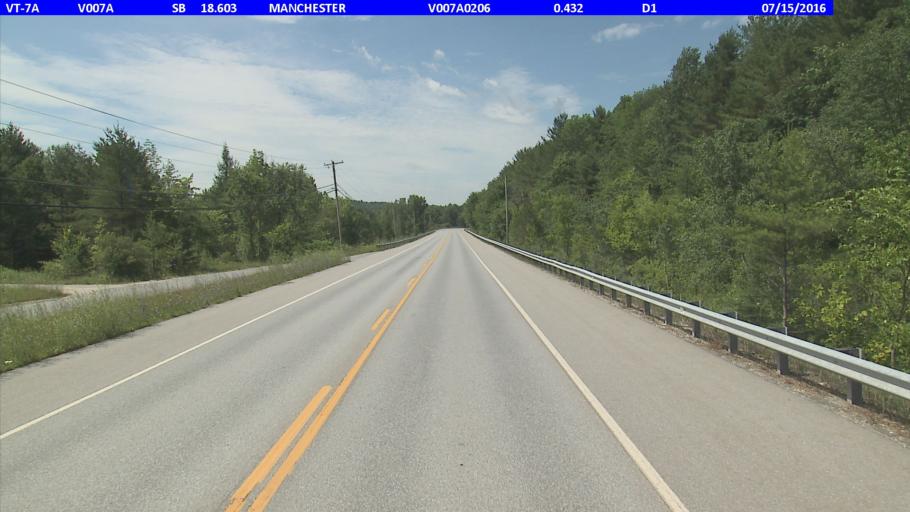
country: US
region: Vermont
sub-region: Bennington County
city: Manchester Center
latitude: 43.1243
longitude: -73.0995
